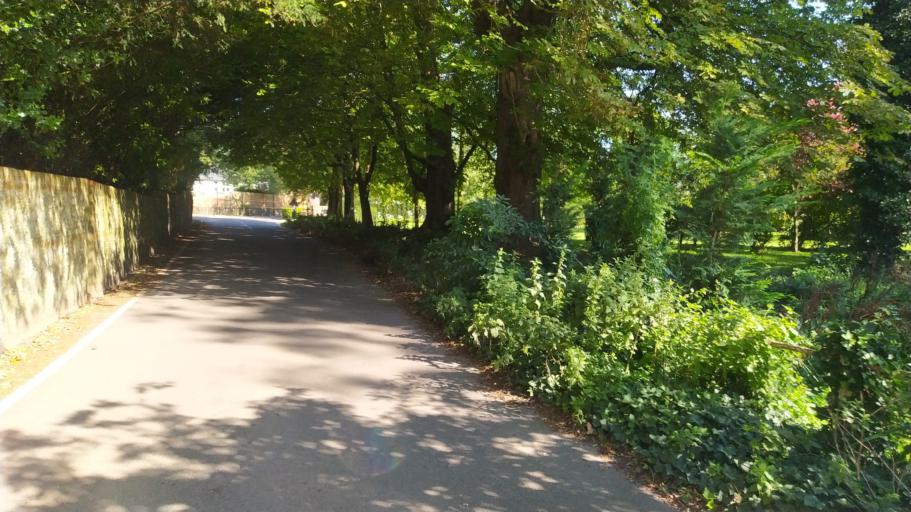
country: GB
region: England
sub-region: Hampshire
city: Abbotts Ann
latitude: 51.1746
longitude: -1.6043
